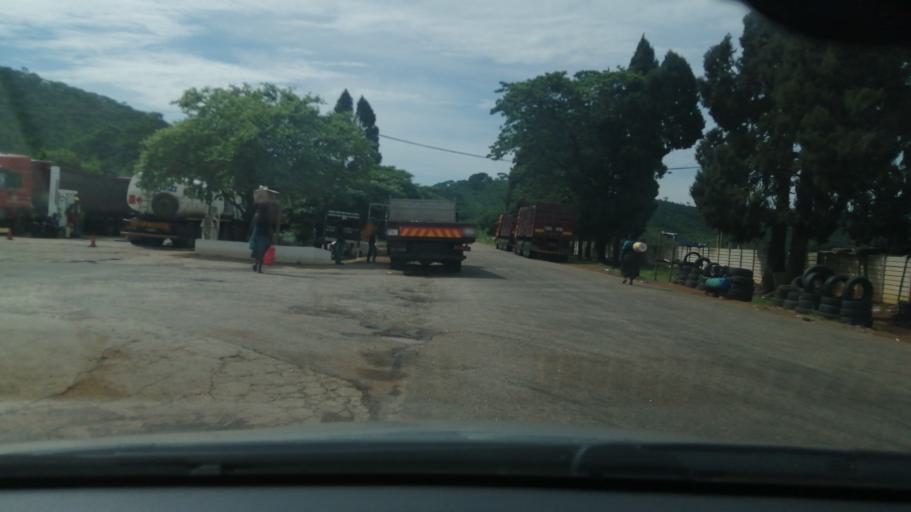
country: ZW
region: Mashonaland West
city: Norton
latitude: -17.8532
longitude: 30.7923
